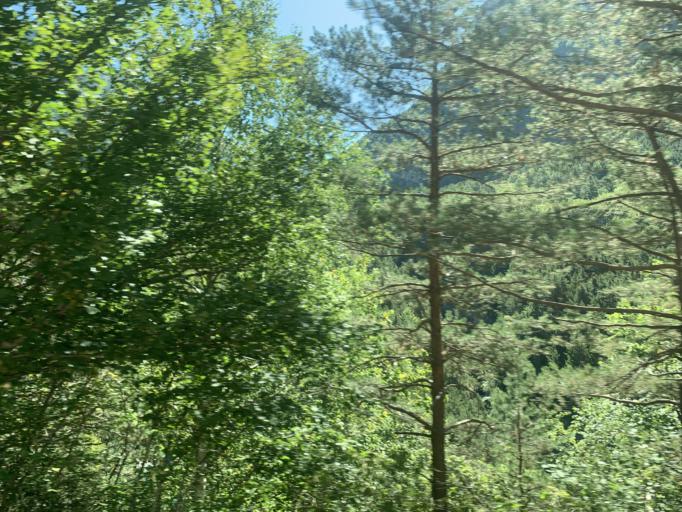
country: ES
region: Aragon
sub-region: Provincia de Huesca
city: Broto
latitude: 42.6516
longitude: -0.1051
